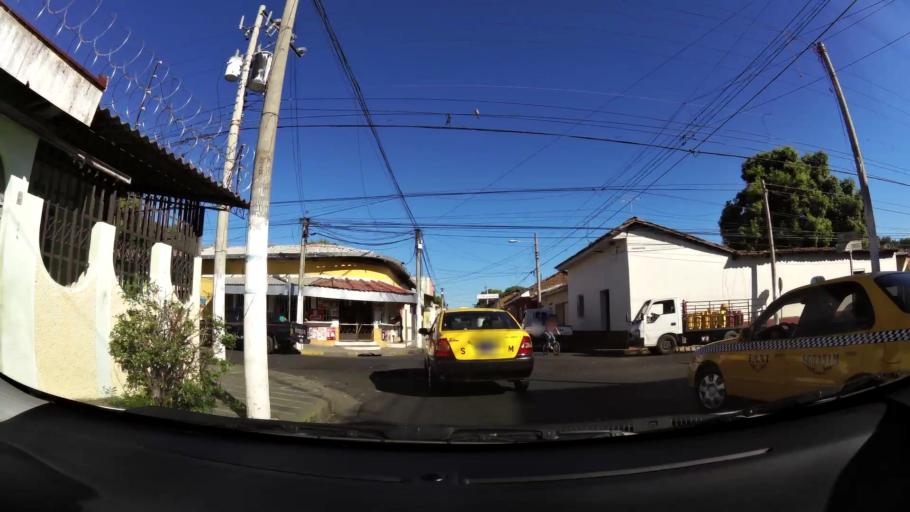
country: SV
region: San Miguel
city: San Miguel
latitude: 13.4745
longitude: -88.1773
